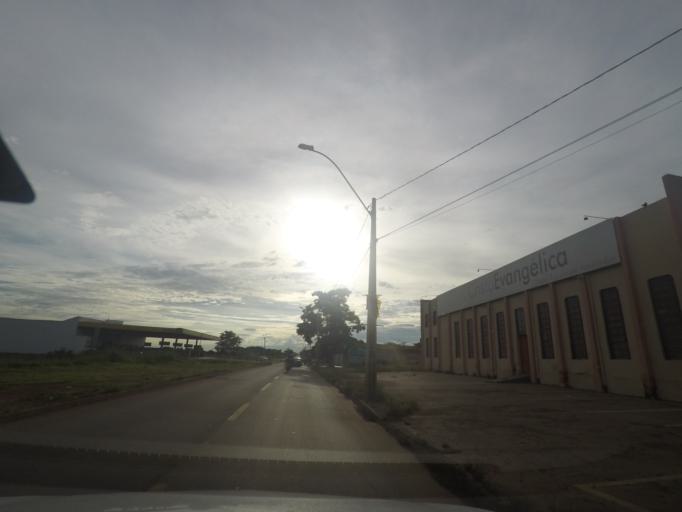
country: BR
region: Goias
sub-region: Goiania
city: Goiania
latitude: -16.6847
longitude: -49.3573
